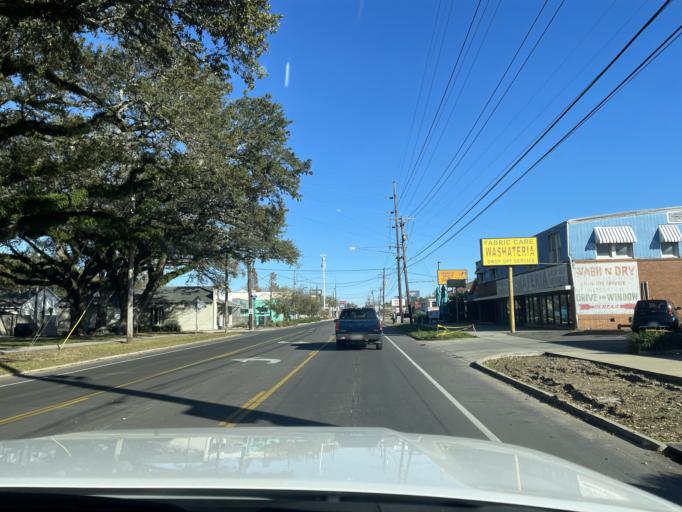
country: US
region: Louisiana
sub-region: East Baton Rouge Parish
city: Baton Rouge
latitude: 30.4441
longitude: -91.1589
